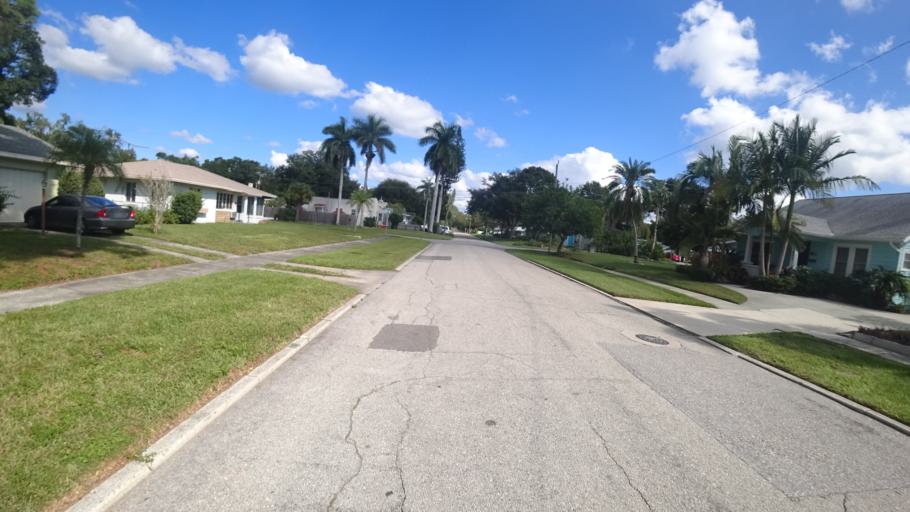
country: US
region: Florida
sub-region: Manatee County
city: Bradenton
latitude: 27.4874
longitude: -82.5859
